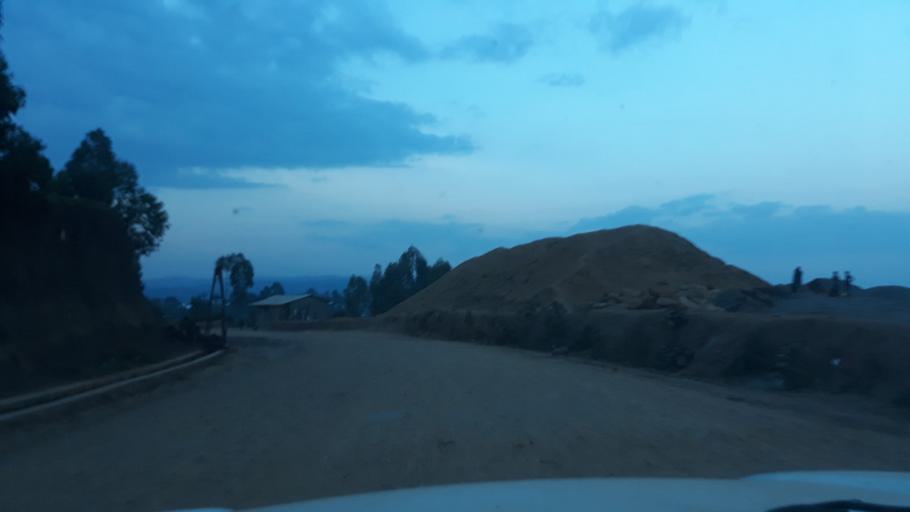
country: CD
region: South Kivu
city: Bukavu
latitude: -2.5609
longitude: 28.8638
